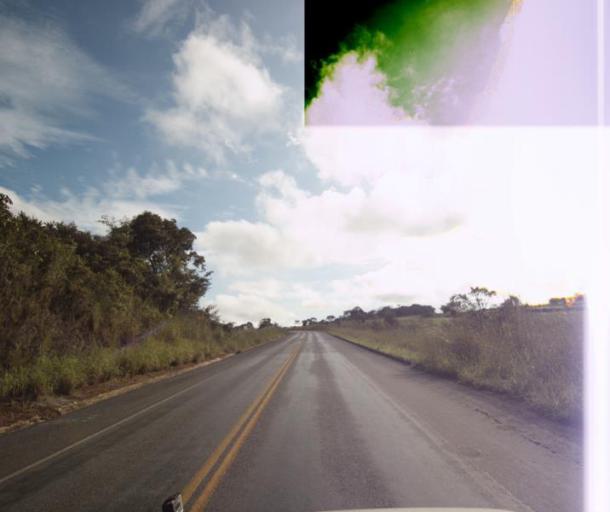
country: BR
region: Goias
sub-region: Padre Bernardo
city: Padre Bernardo
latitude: -15.4839
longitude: -48.6173
